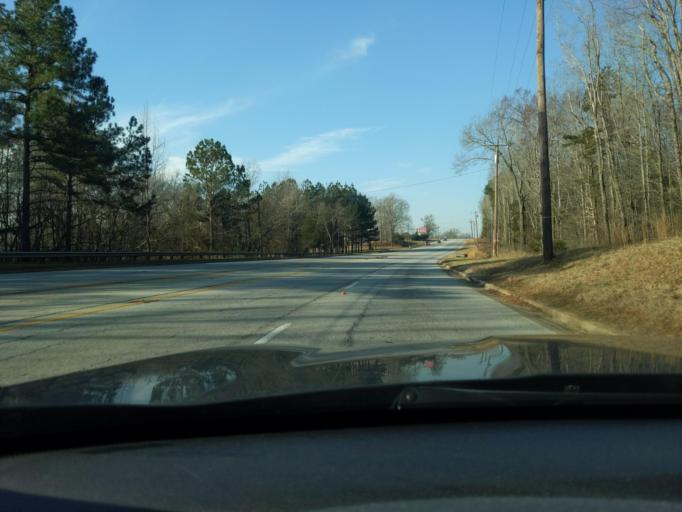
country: US
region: South Carolina
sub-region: Greenwood County
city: Greenwood
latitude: 34.1921
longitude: -82.2147
